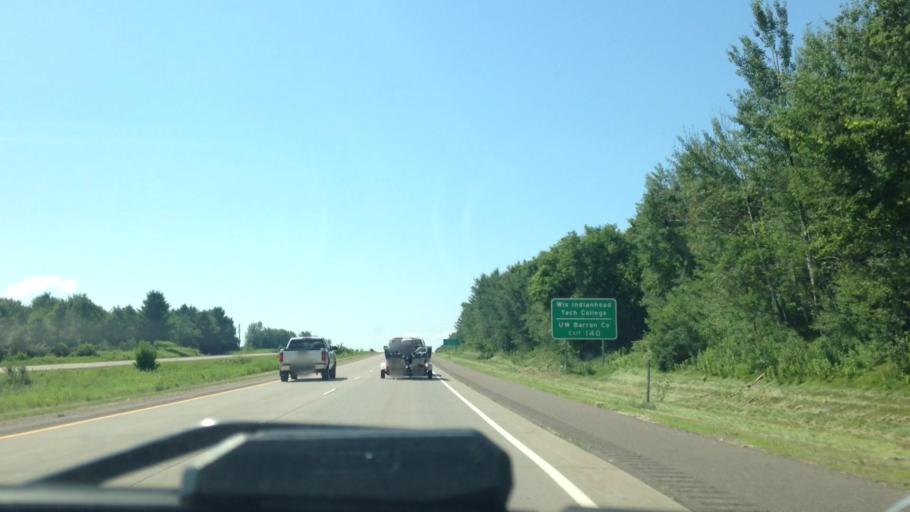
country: US
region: Wisconsin
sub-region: Barron County
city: Rice Lake
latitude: 45.4914
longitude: -91.7634
